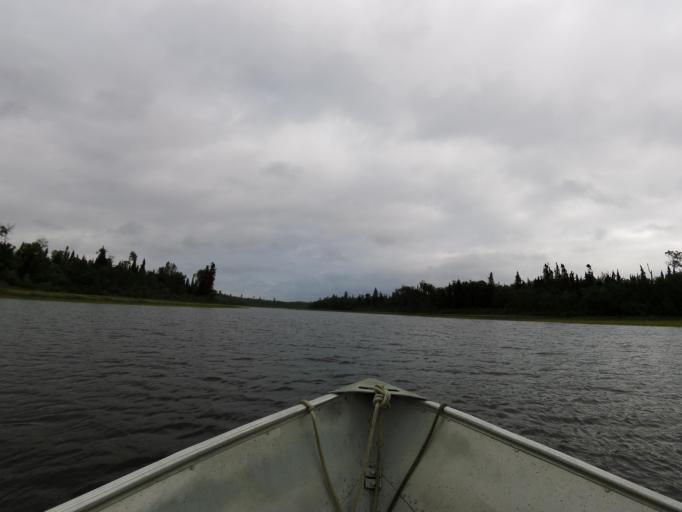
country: CA
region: Ontario
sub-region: Rainy River District
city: Atikokan
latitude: 49.5926
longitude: -91.3597
